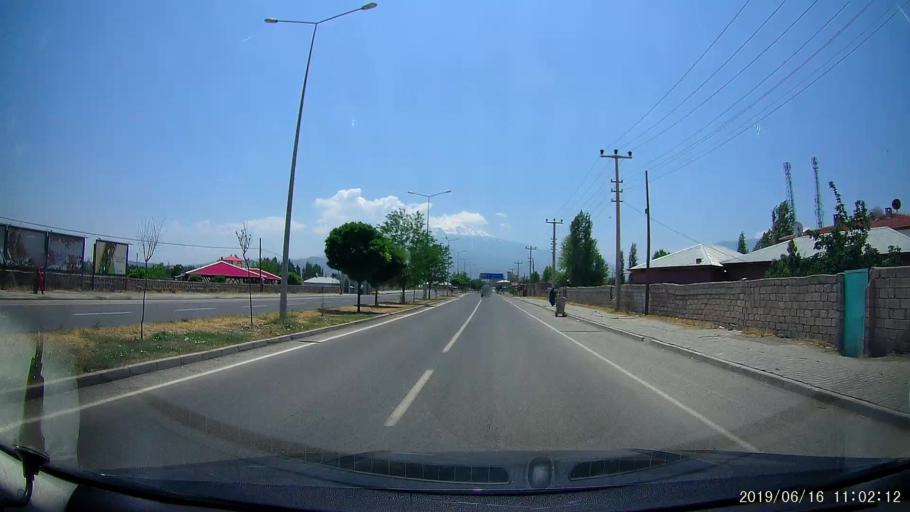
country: TR
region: Igdir
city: Igdir
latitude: 39.9087
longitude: 44.0575
